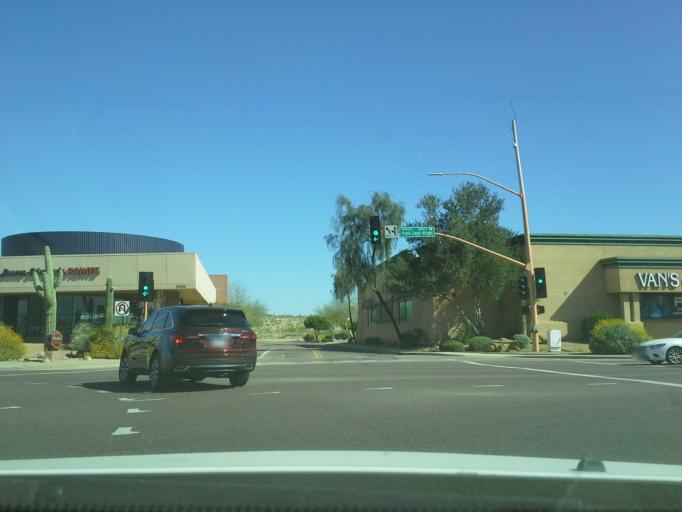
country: US
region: Arizona
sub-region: Maricopa County
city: Paradise Valley
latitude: 33.6301
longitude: -111.8931
